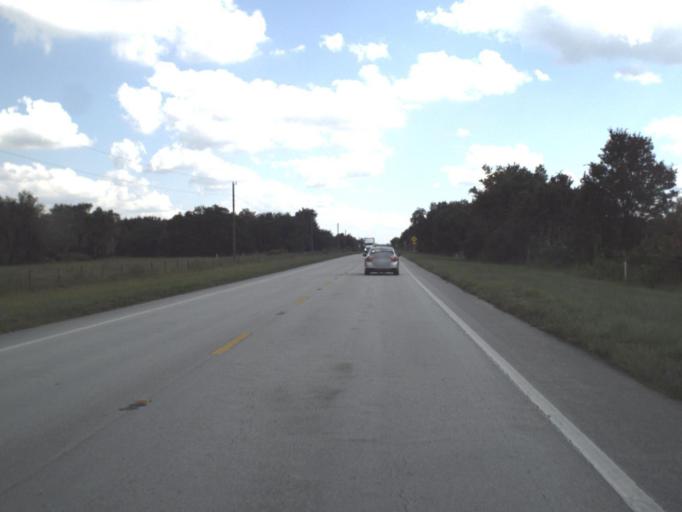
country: US
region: Florida
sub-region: Highlands County
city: Lake Placid
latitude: 27.4037
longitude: -81.1715
